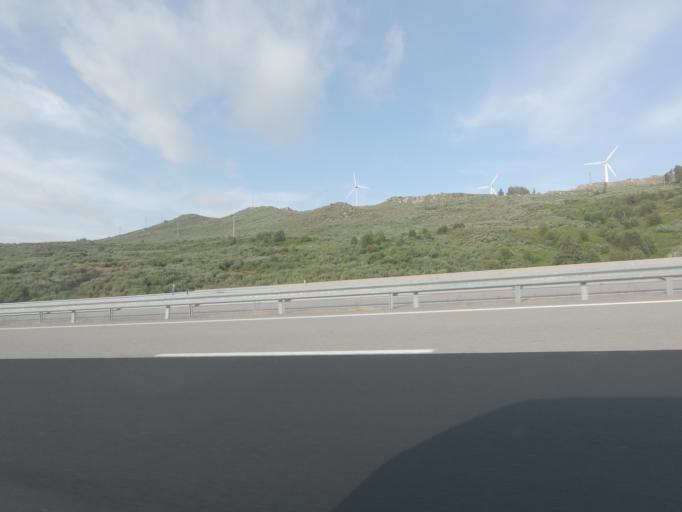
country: PT
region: Vila Real
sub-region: Vila Pouca de Aguiar
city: Vila Pouca de Aguiar
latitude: 41.4617
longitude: -7.6438
